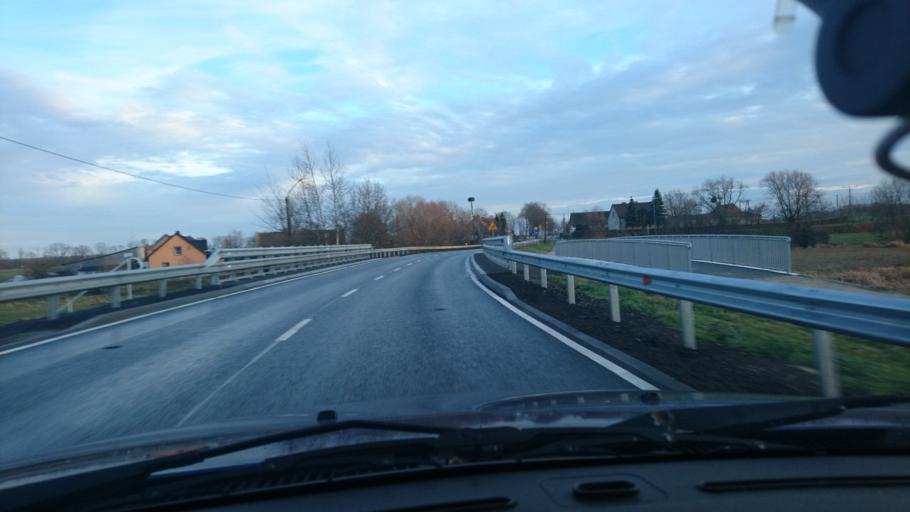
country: PL
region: Greater Poland Voivodeship
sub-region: Powiat kepinski
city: Opatow
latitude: 51.1646
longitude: 18.1511
